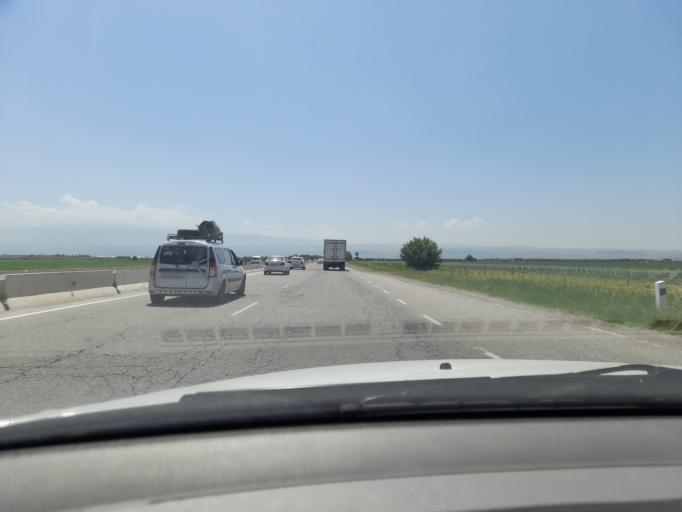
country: UZ
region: Jizzax
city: Jizzax
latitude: 40.1220
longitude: 67.9491
